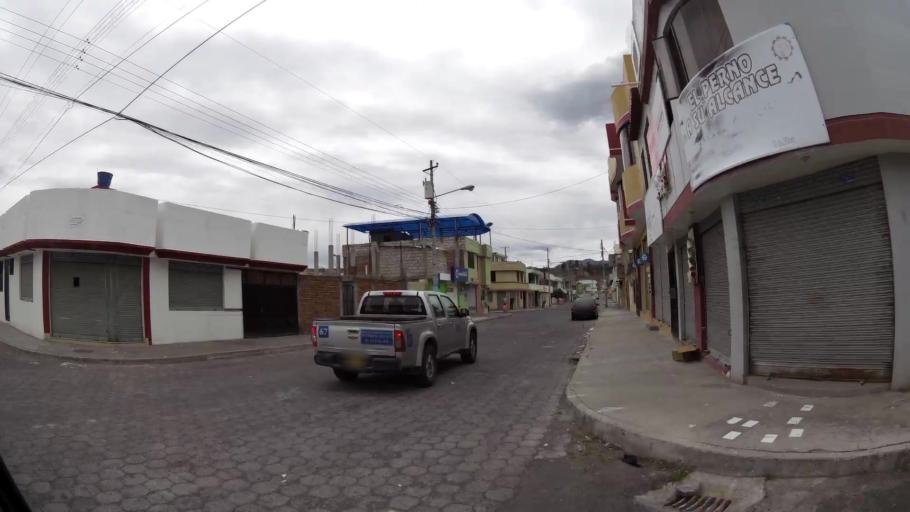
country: EC
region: Cotopaxi
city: Latacunga
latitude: -0.9661
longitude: -78.6118
